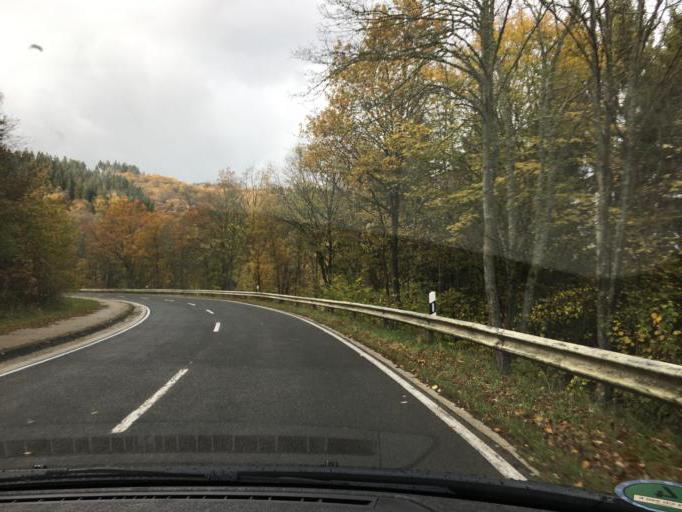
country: DE
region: North Rhine-Westphalia
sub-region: Regierungsbezirk Koln
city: Simmerath
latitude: 50.6020
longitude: 6.3802
